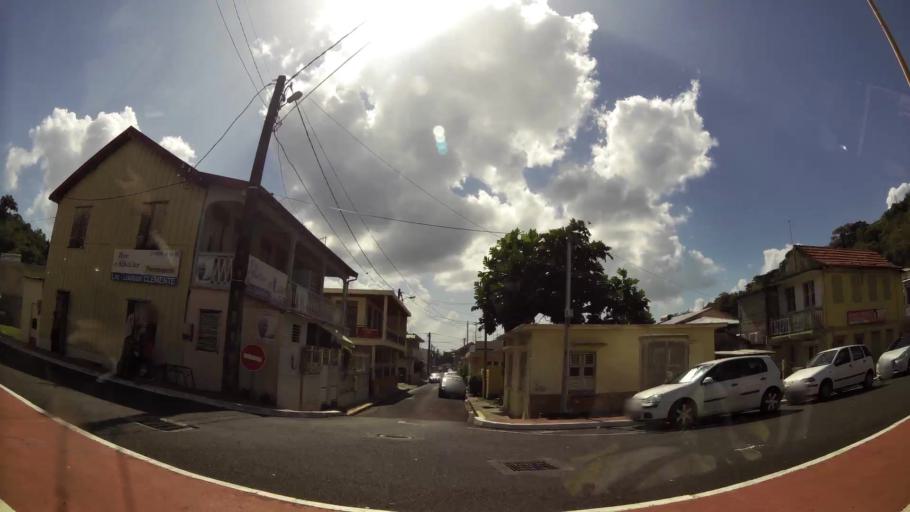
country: MQ
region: Martinique
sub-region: Martinique
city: Fort-de-France
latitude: 14.6281
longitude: -61.1111
